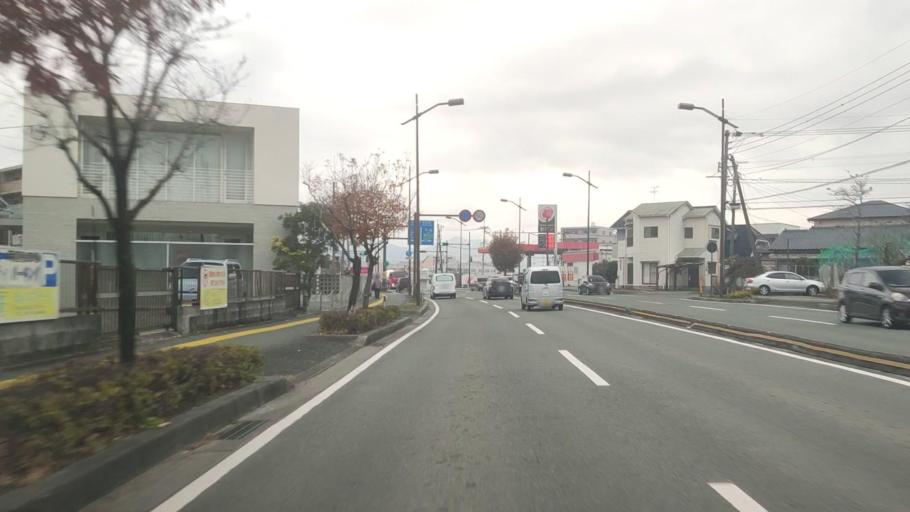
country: JP
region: Kumamoto
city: Kumamoto
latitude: 32.8068
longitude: 130.7514
